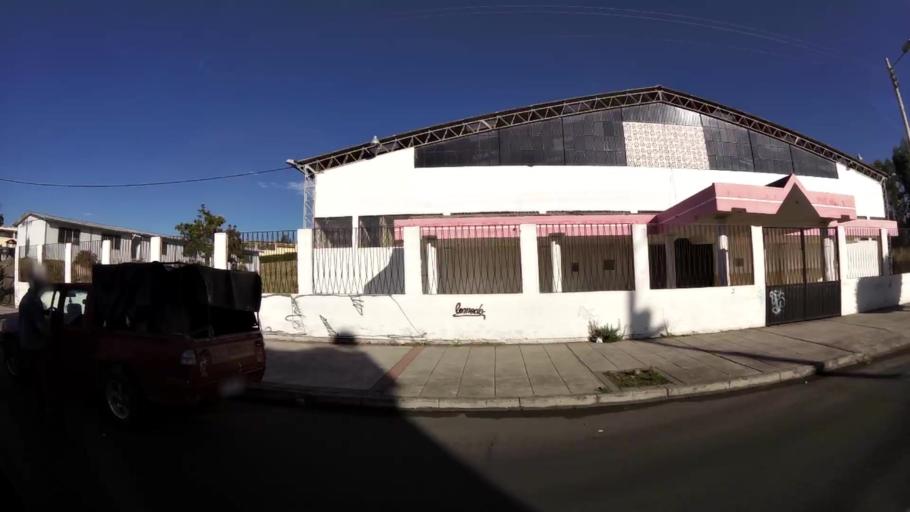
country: EC
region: Chimborazo
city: Riobamba
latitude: -1.6584
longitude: -78.6463
